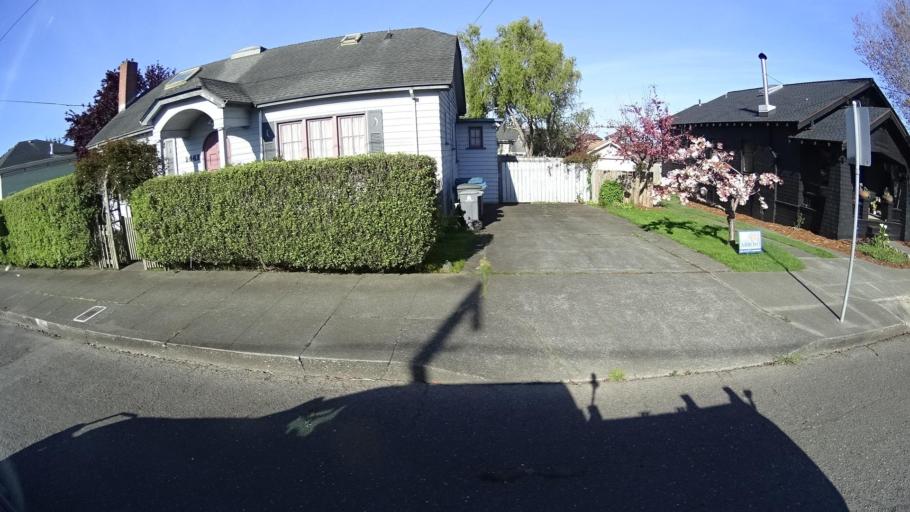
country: US
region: California
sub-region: Humboldt County
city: Eureka
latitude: 40.7941
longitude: -124.1631
